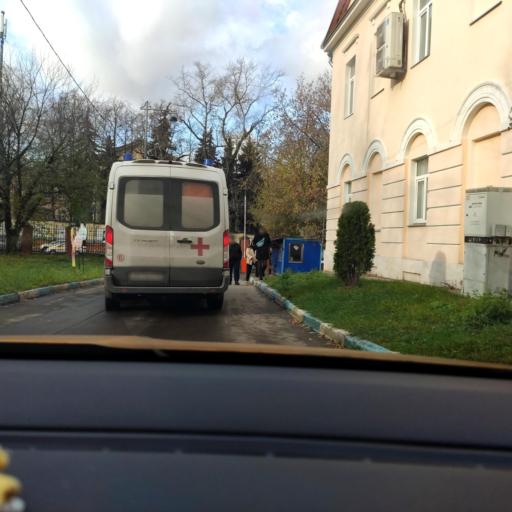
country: RU
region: Moscow
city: Lefortovo
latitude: 55.7687
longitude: 37.7019
